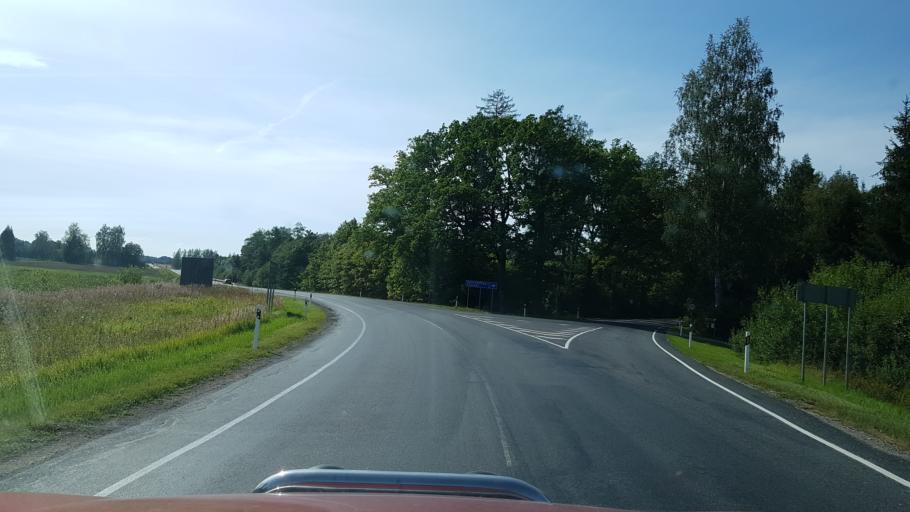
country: EE
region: Viljandimaa
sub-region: Viljandi linn
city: Viljandi
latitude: 58.3257
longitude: 25.4853
